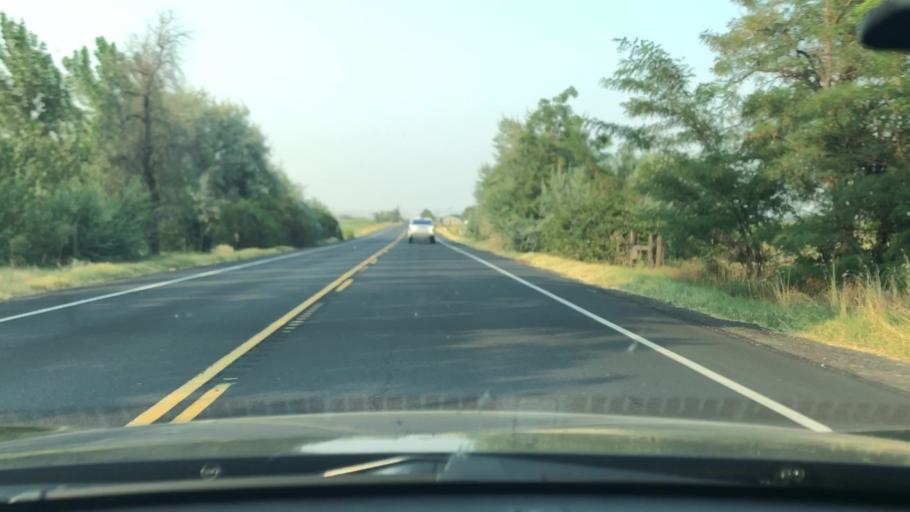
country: US
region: Oregon
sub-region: Umatilla County
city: Hermiston
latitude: 45.8898
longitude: -119.1877
